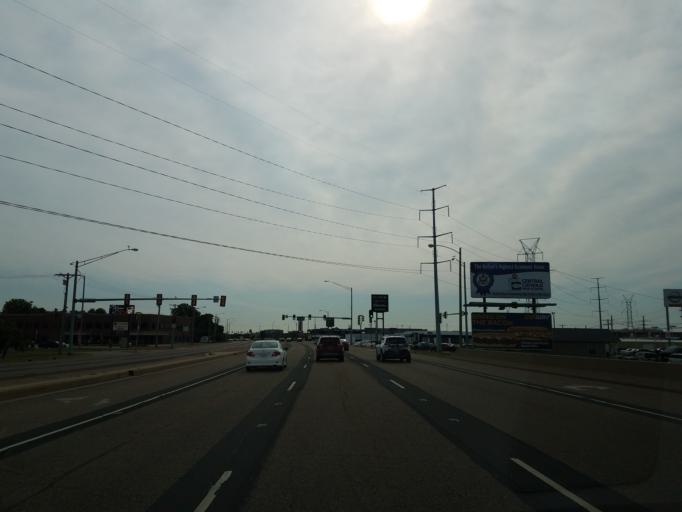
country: US
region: Illinois
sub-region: McLean County
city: Bloomington
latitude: 40.4598
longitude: -88.9675
